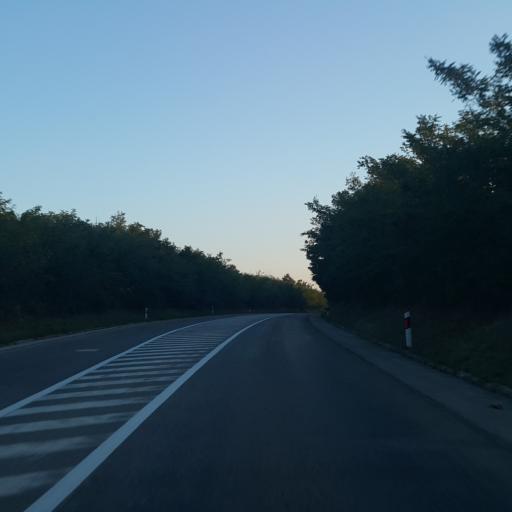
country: RS
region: Central Serbia
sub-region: Zajecarski Okrug
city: Zajecar
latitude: 44.0185
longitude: 22.3001
